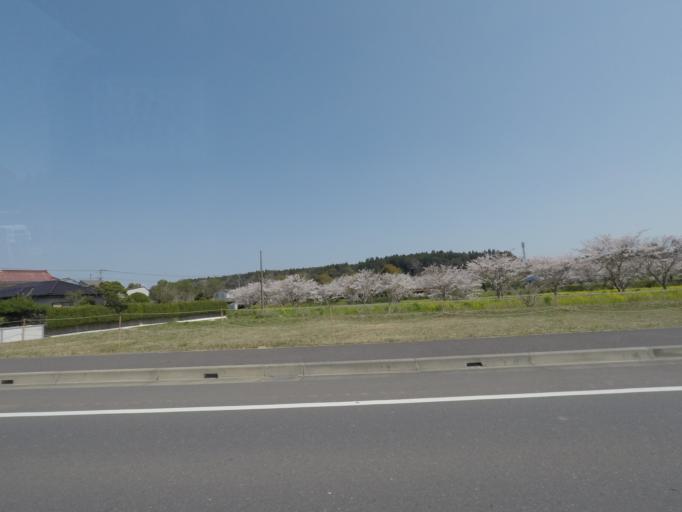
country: JP
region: Chiba
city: Yokaichiba
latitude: 35.7404
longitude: 140.4739
